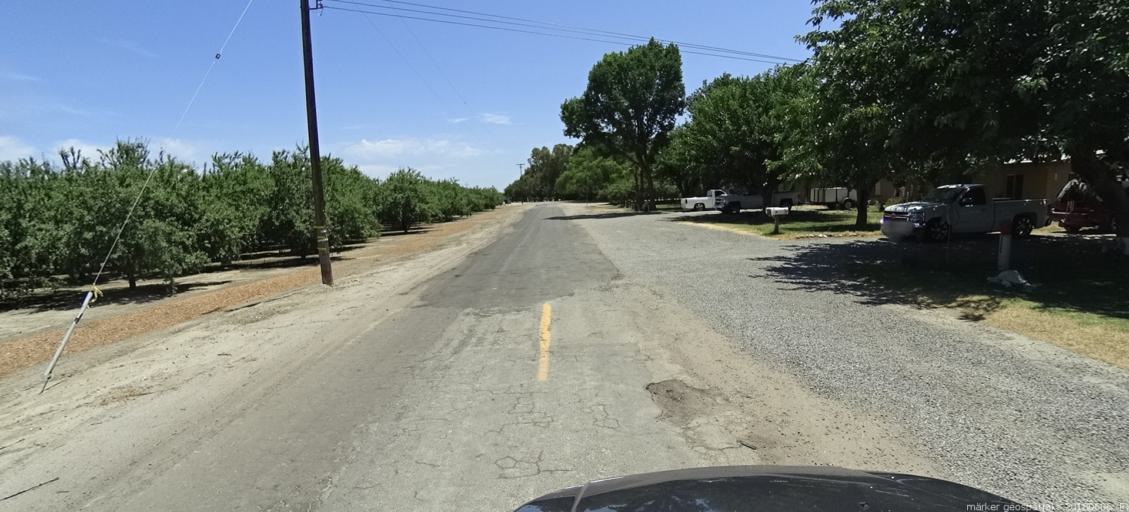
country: US
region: California
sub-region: Fresno County
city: Mendota
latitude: 36.8066
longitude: -120.3533
